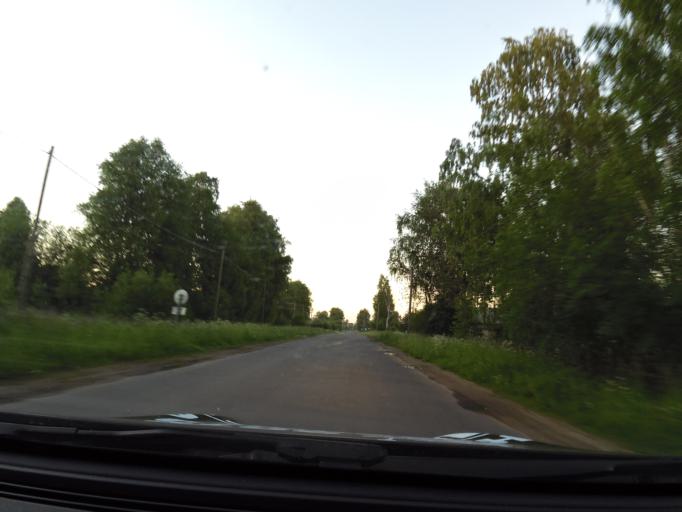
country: RU
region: Leningrad
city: Voznesen'ye
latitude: 60.8282
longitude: 35.7388
